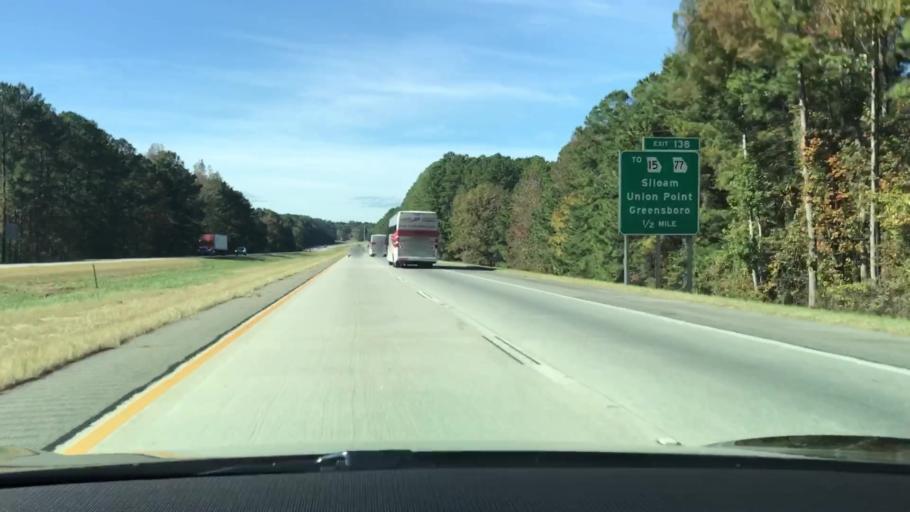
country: US
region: Georgia
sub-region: Greene County
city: Union Point
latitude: 33.5472
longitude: -83.0665
